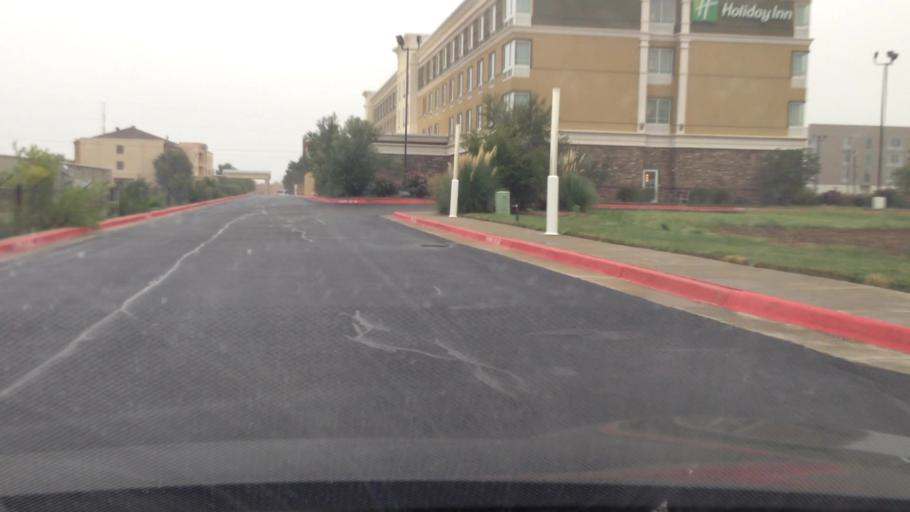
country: US
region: Texas
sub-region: Potter County
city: Amarillo
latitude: 35.1905
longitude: -101.9304
